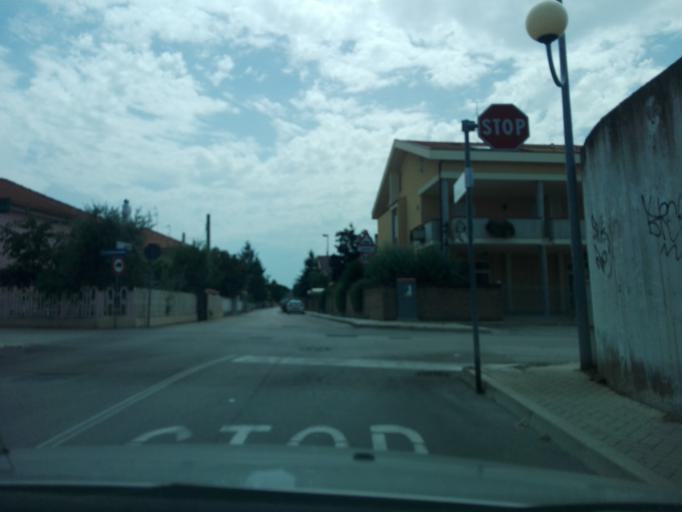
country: IT
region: Abruzzo
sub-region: Provincia di Pescara
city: Montesilvano Marina
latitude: 42.4993
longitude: 14.1297
